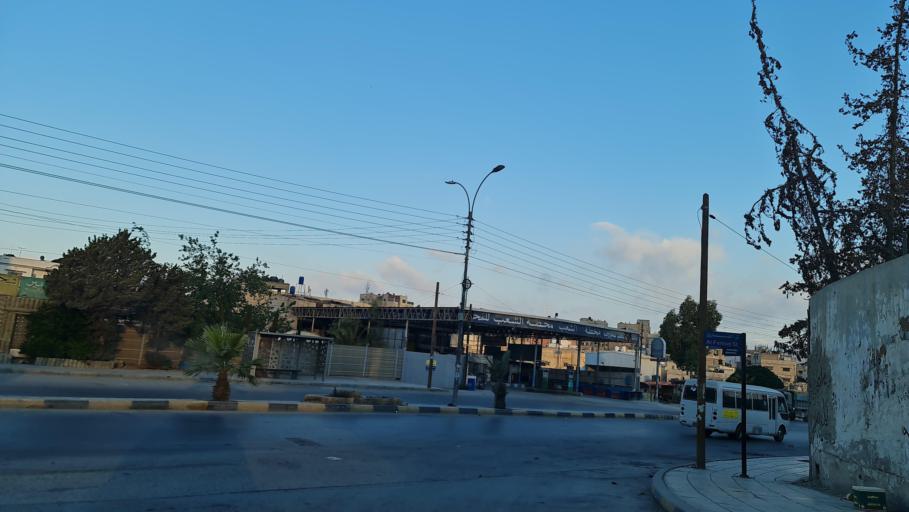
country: JO
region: Zarqa
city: Zarqa
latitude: 32.0748
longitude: 36.0786
